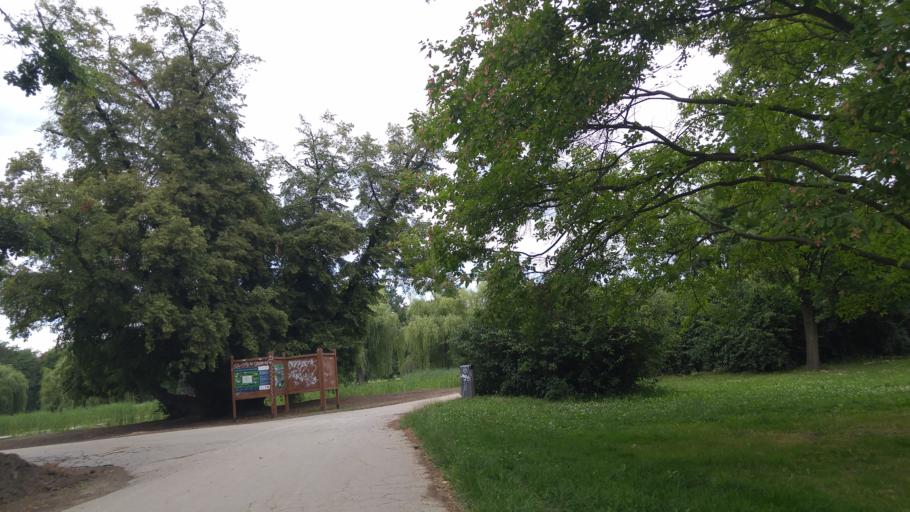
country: CZ
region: Praha
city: Prague
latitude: 50.1066
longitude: 14.4222
